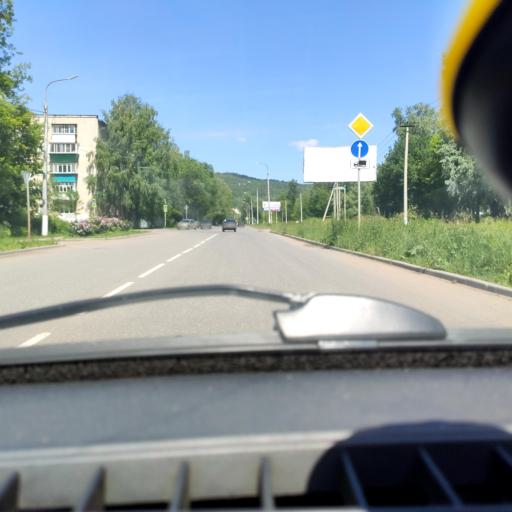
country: RU
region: Samara
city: Zhigulevsk
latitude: 53.3995
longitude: 49.5107
